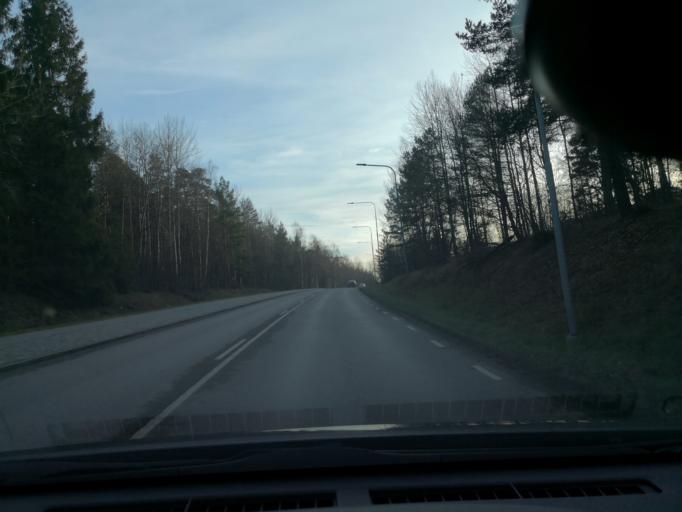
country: SE
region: Vaestmanland
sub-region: Vasteras
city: Vasteras
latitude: 59.6156
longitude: 16.5059
